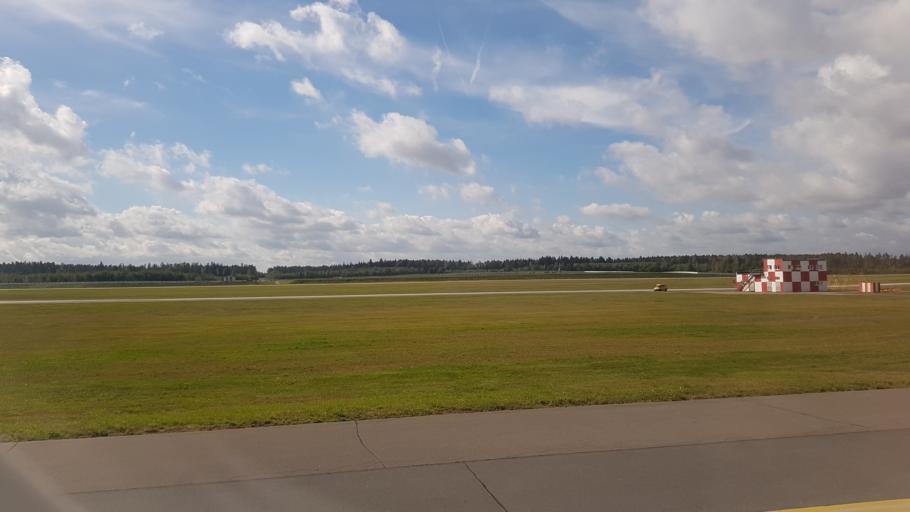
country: BY
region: Minsk
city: Smilavichy
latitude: 53.8869
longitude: 28.0324
